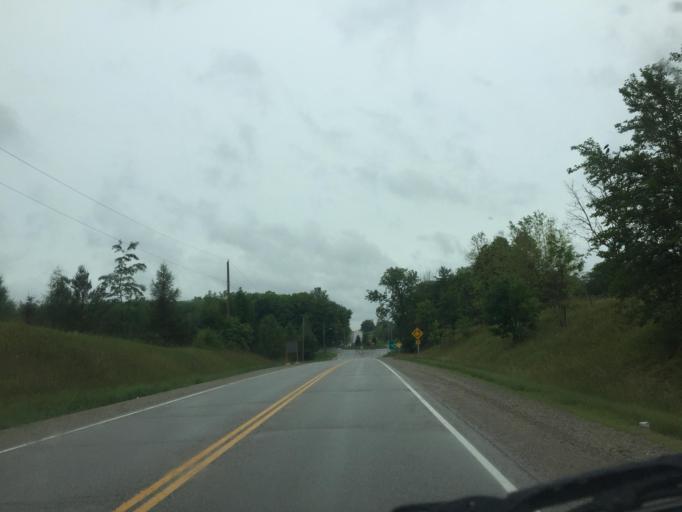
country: CA
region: Ontario
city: Cambridge
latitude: 43.4410
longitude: -80.2648
